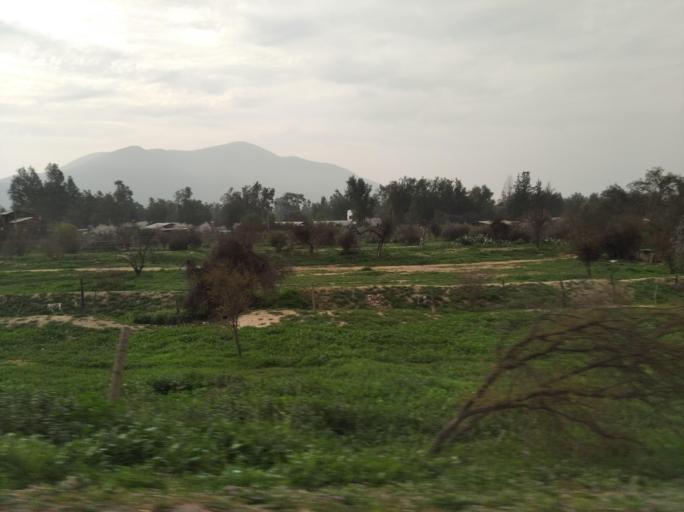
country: CL
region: Santiago Metropolitan
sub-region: Provincia de Chacabuco
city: Lampa
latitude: -33.2660
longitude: -70.8962
